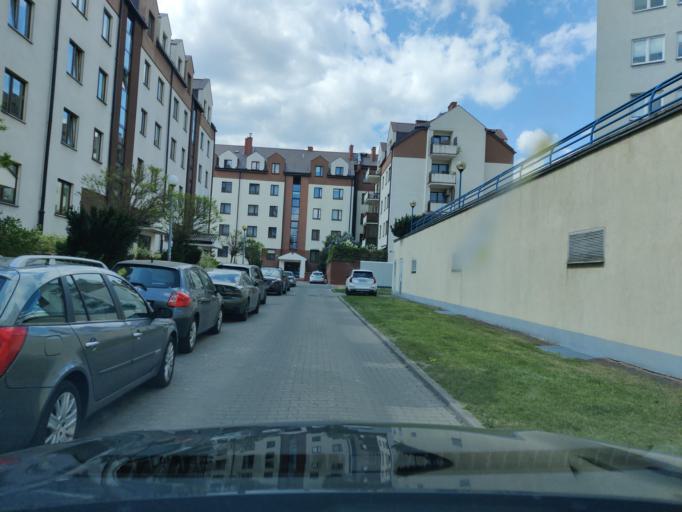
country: PL
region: Masovian Voivodeship
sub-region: Warszawa
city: Kabaty
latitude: 52.1309
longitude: 21.0711
